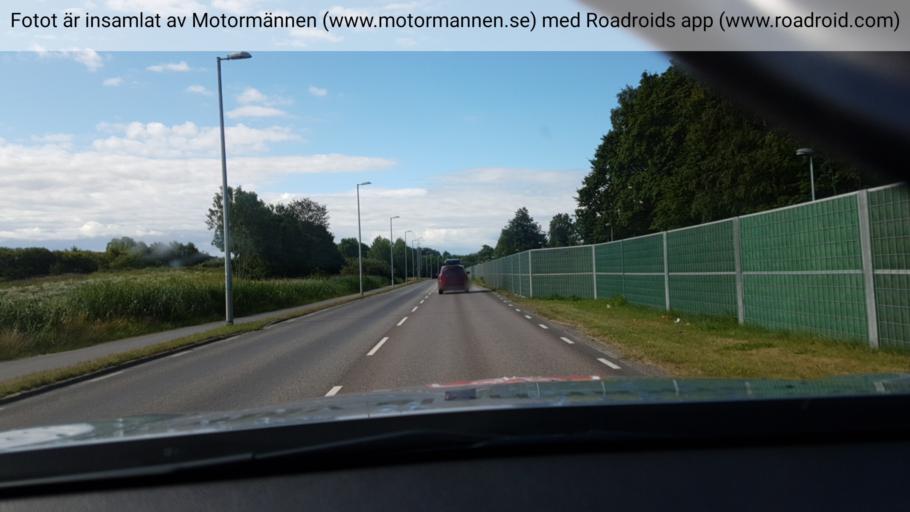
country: SE
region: Vaestra Goetaland
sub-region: Goteborg
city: Majorna
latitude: 57.6422
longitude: 11.9155
